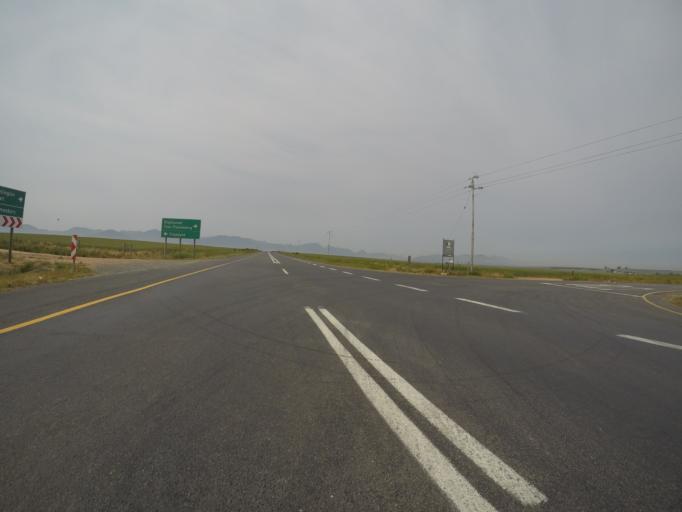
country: ZA
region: Western Cape
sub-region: Cape Winelands District Municipality
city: Noorder-Paarl
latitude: -33.5673
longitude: 18.8875
